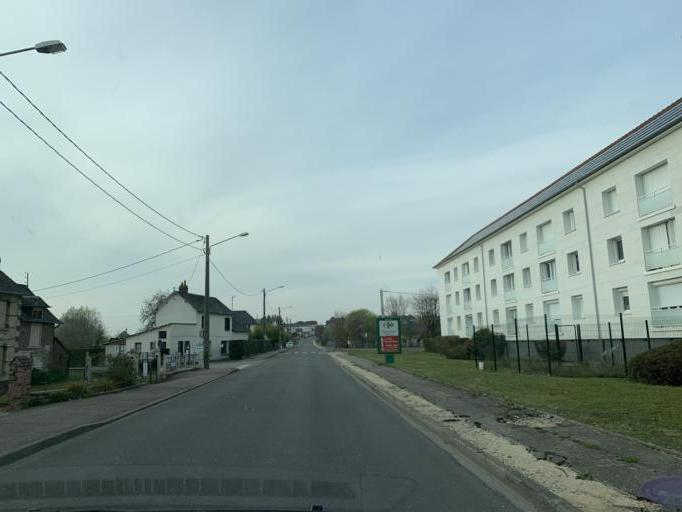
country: FR
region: Haute-Normandie
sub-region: Departement de la Seine-Maritime
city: La Mailleraye-sur-Seine
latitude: 49.4785
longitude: 0.7746
